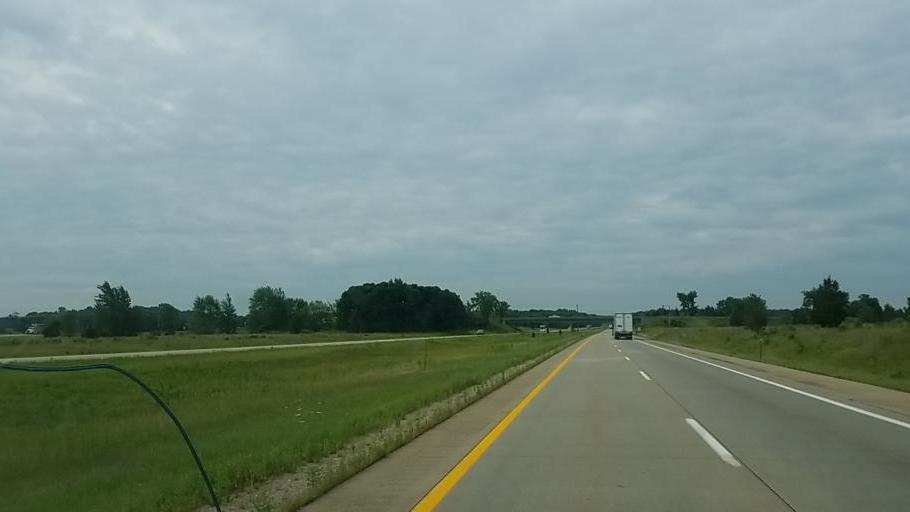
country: US
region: Michigan
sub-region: Branch County
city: Coldwater
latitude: 41.9887
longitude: -84.9722
